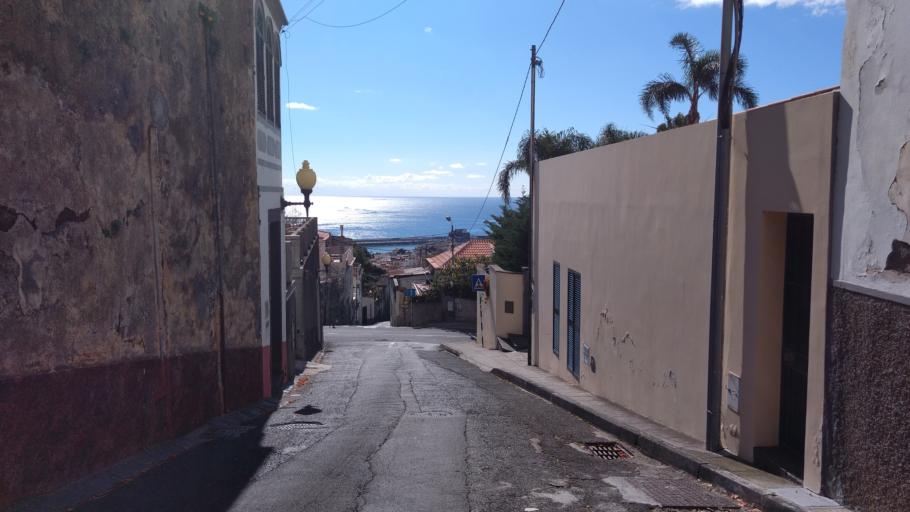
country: PT
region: Madeira
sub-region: Funchal
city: Nossa Senhora do Monte
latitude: 32.6576
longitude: -16.9074
